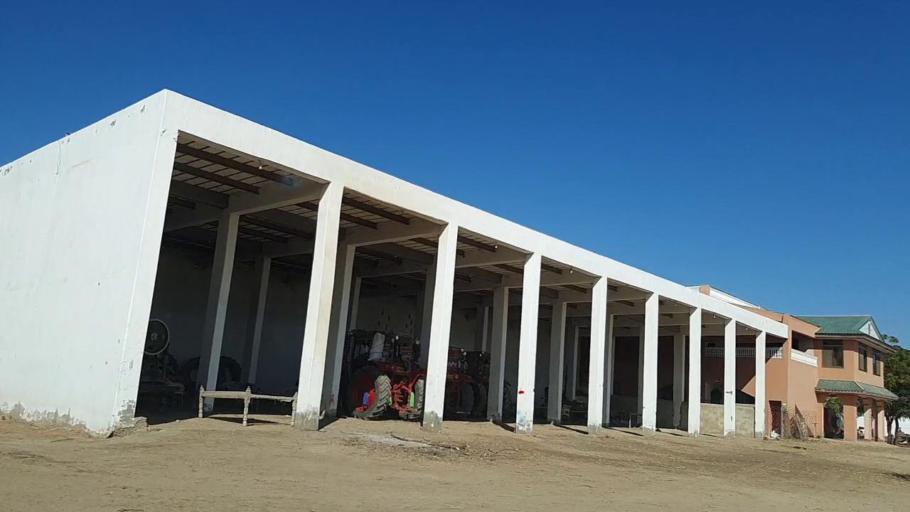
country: PK
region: Sindh
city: Dhoro Naro
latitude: 25.5369
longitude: 69.4809
